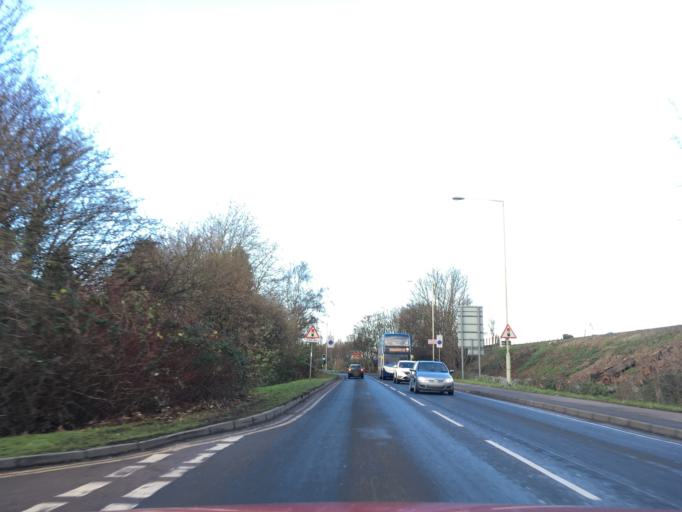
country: GB
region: England
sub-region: Gloucestershire
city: Gloucester
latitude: 51.8693
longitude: -2.2450
